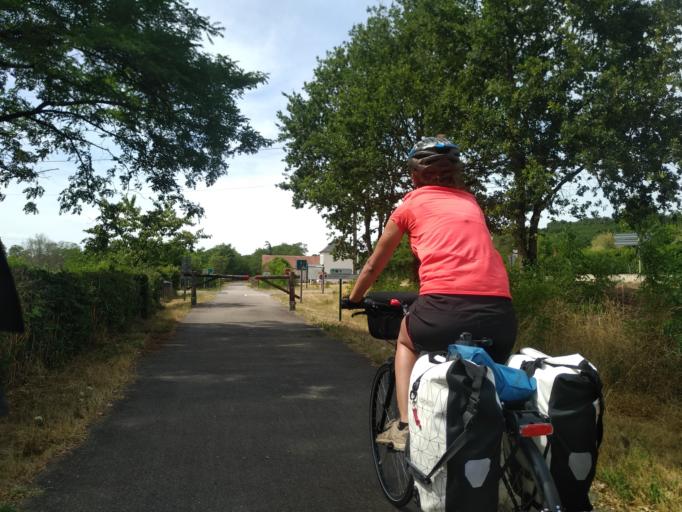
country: FR
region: Auvergne
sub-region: Departement de l'Allier
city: Diou
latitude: 46.5410
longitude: 3.7492
